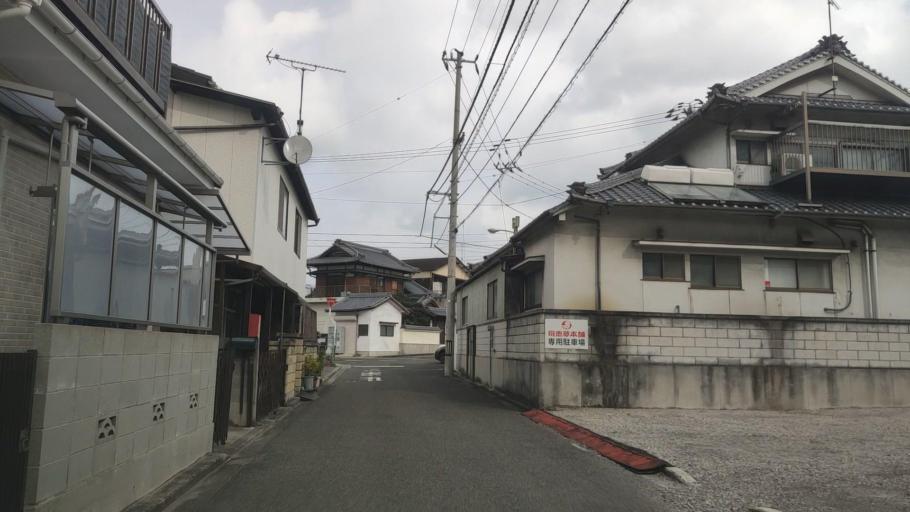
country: JP
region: Ehime
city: Saijo
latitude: 34.0614
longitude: 133.0176
